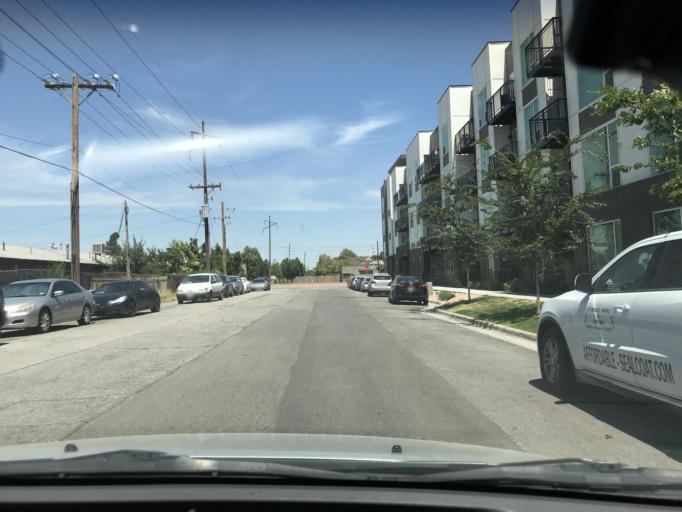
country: US
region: Utah
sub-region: Salt Lake County
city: Salt Lake City
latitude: 40.7706
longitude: -111.9439
